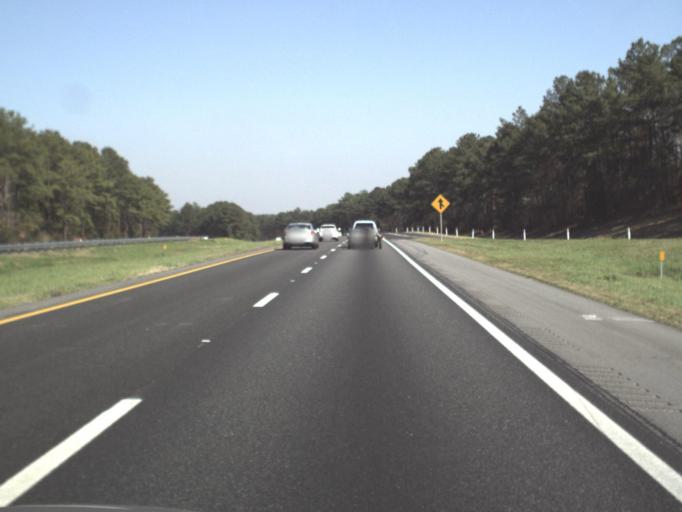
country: US
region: Florida
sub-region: Gadsden County
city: Chattahoochee
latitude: 30.6179
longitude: -84.8195
